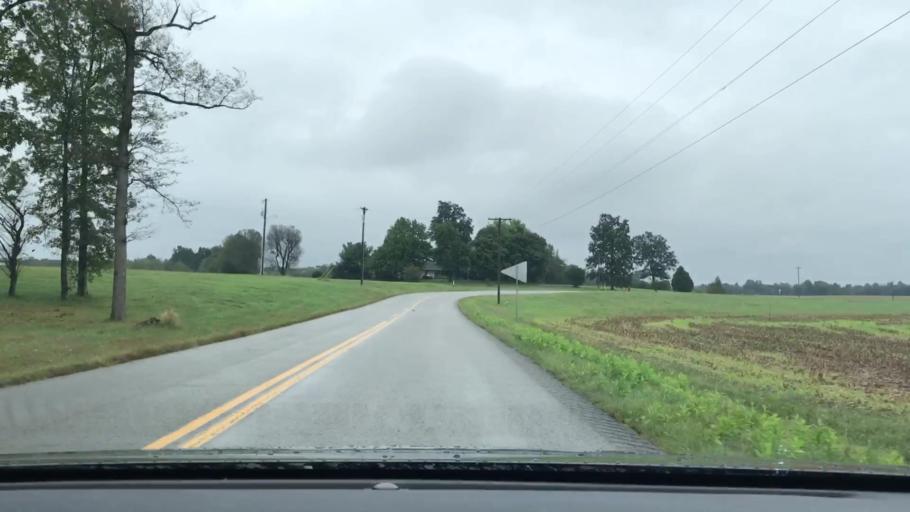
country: US
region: Kentucky
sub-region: McLean County
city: Calhoun
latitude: 37.4708
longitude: -87.2351
